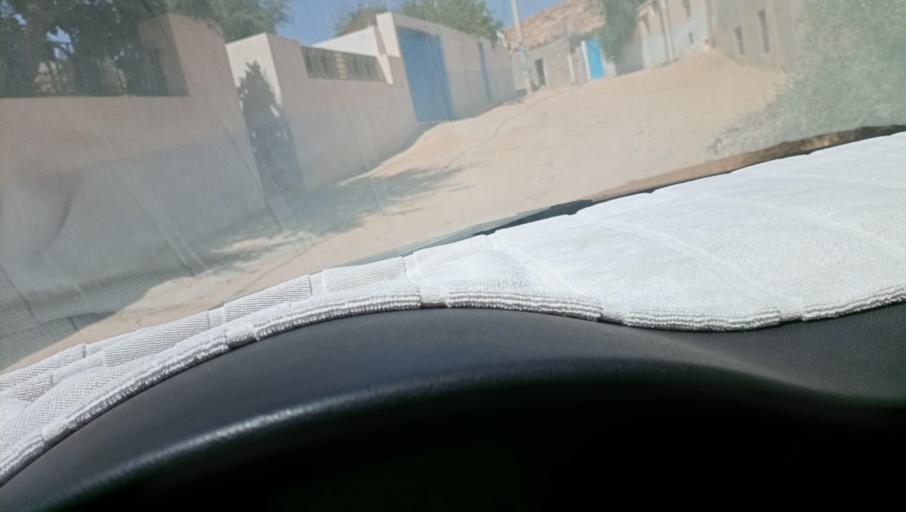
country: TN
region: Tataouine
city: Tataouine
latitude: 32.8577
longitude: 10.4741
